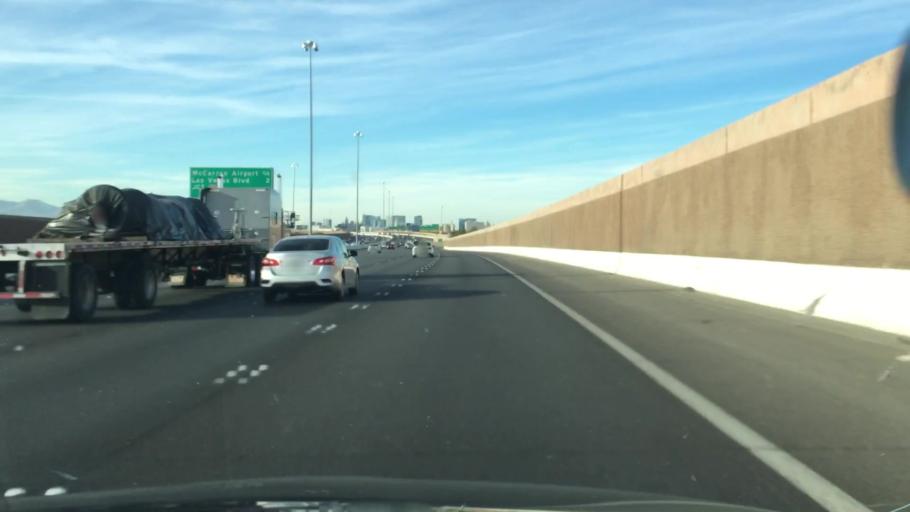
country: US
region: Nevada
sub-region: Clark County
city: Paradise
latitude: 36.0512
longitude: -115.1361
